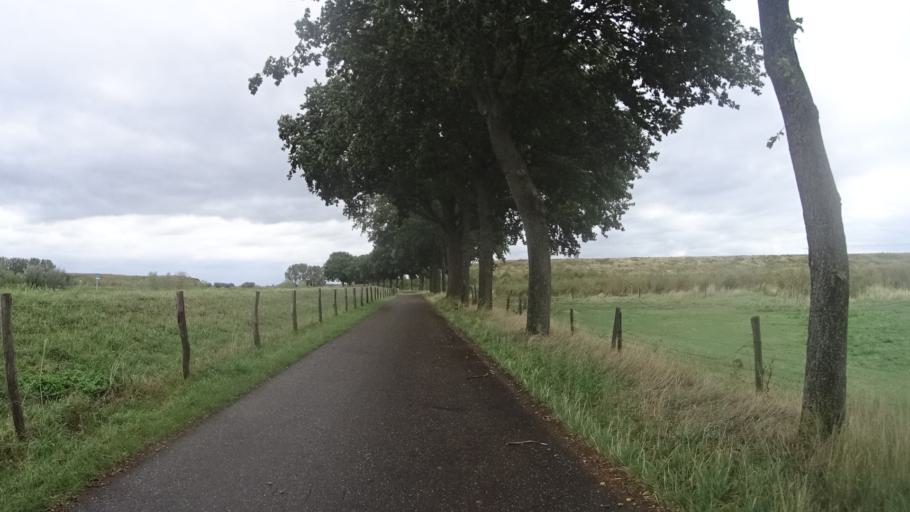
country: NL
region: Limburg
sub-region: Gemeente Sittard-Geleen
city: Born
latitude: 51.0484
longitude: 5.7886
